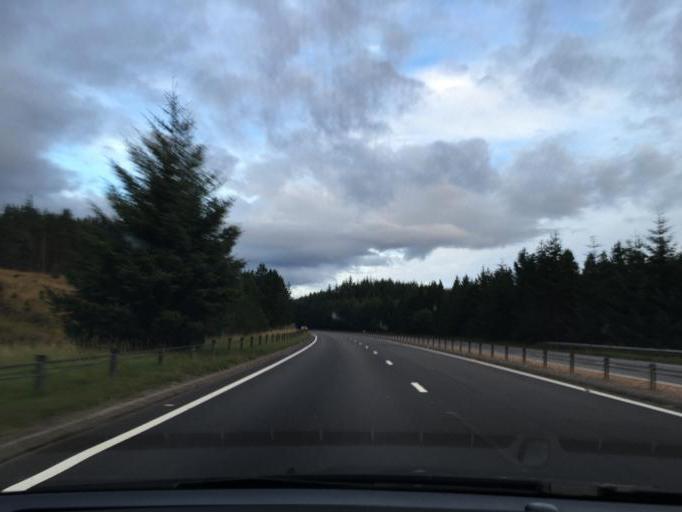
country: GB
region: Scotland
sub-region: Highland
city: Inverness
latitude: 57.3881
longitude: -4.1195
